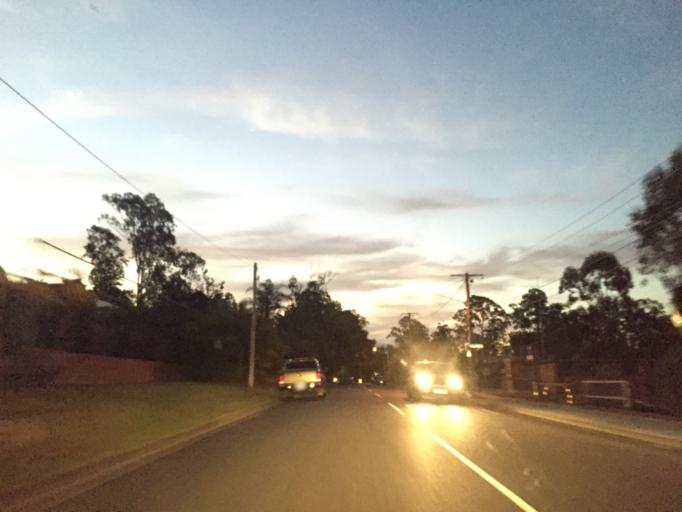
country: AU
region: Queensland
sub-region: Moreton Bay
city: Ferny Hills
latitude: -27.4485
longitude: 152.9420
